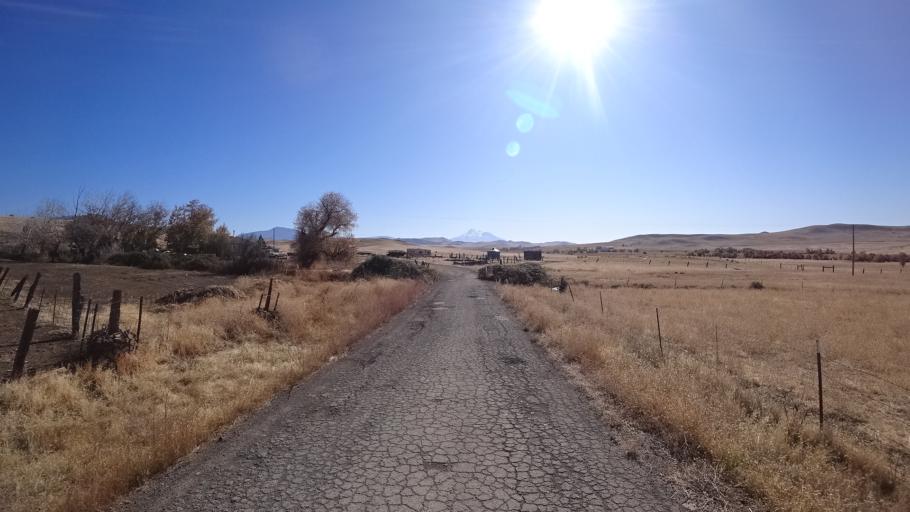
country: US
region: California
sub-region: Siskiyou County
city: Montague
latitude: 41.8452
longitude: -122.4442
